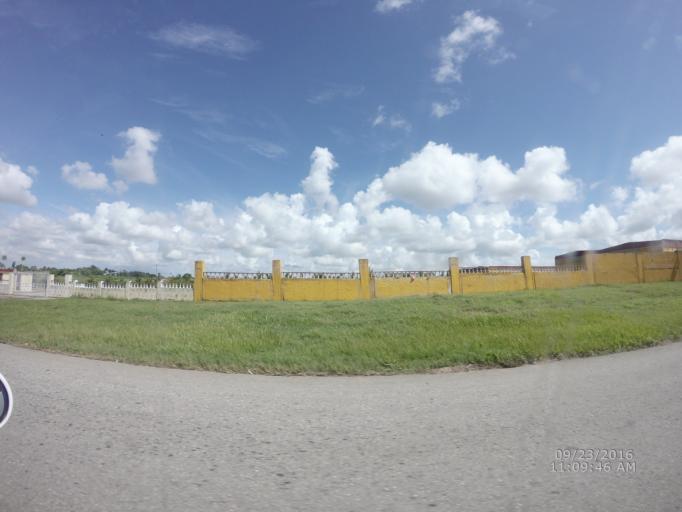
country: CU
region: La Habana
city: Arroyo Naranjo
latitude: 23.0189
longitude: -82.2494
